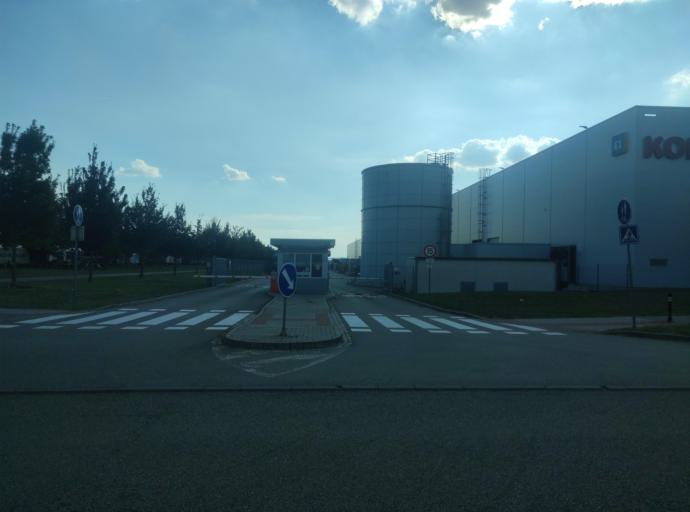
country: CZ
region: South Moravian
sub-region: Mesto Brno
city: Brno
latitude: 49.1800
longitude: 16.6618
